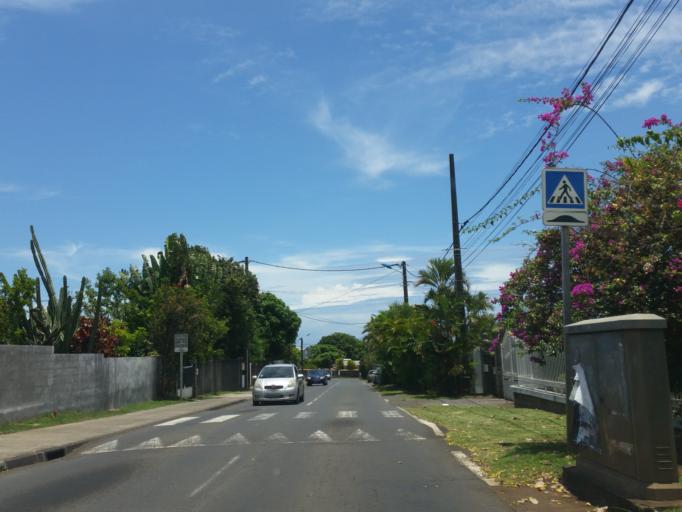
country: RE
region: Reunion
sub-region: Reunion
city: Sainte-Marie
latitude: -20.9057
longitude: 55.5222
